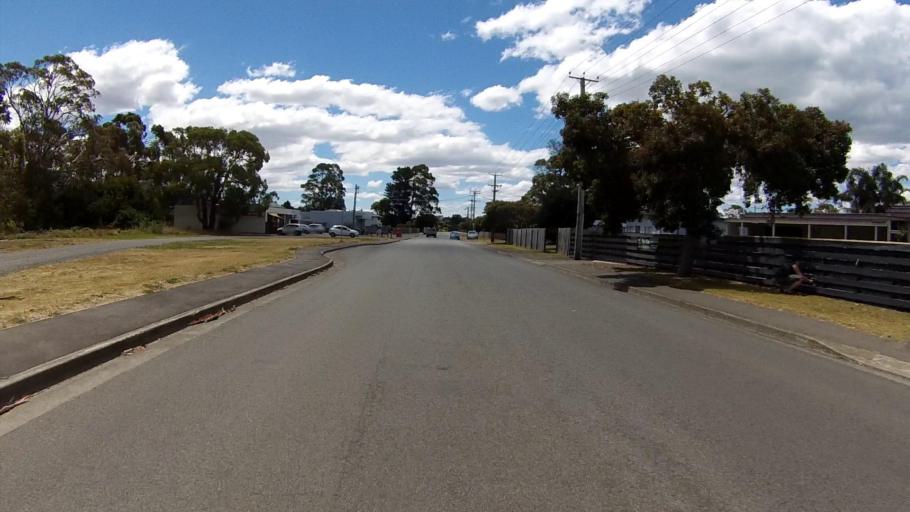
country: AU
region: Tasmania
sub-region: Clarence
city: Lauderdale
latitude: -42.9094
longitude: 147.4924
